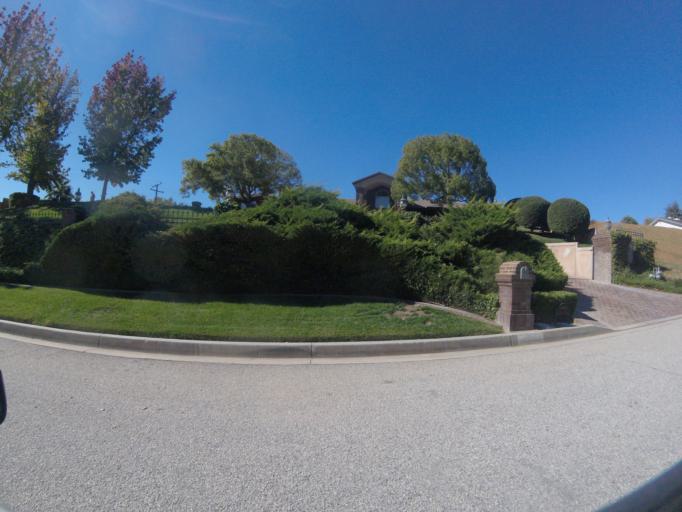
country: US
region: California
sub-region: San Bernardino County
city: Mentone
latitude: 34.0186
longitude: -117.1235
